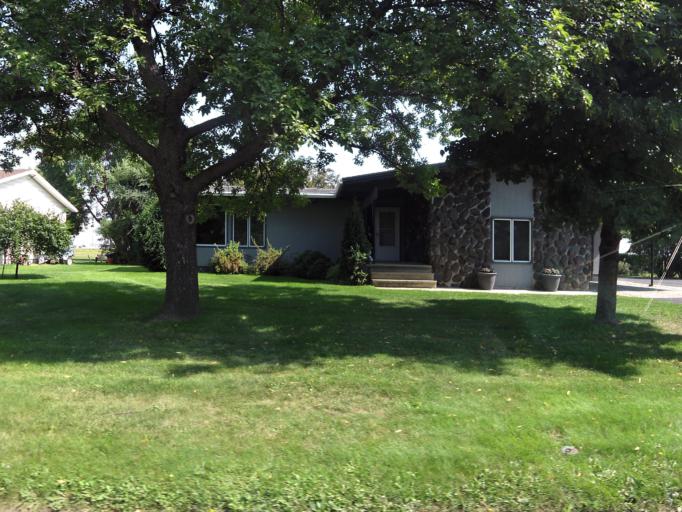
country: US
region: North Dakota
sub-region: Walsh County
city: Grafton
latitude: 48.4104
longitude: -97.3969
